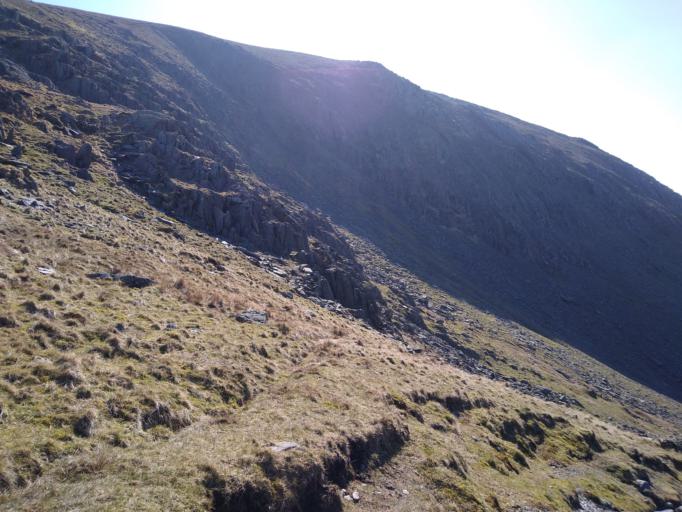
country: GB
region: England
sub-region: Cumbria
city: Ambleside
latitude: 54.3743
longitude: -3.1307
